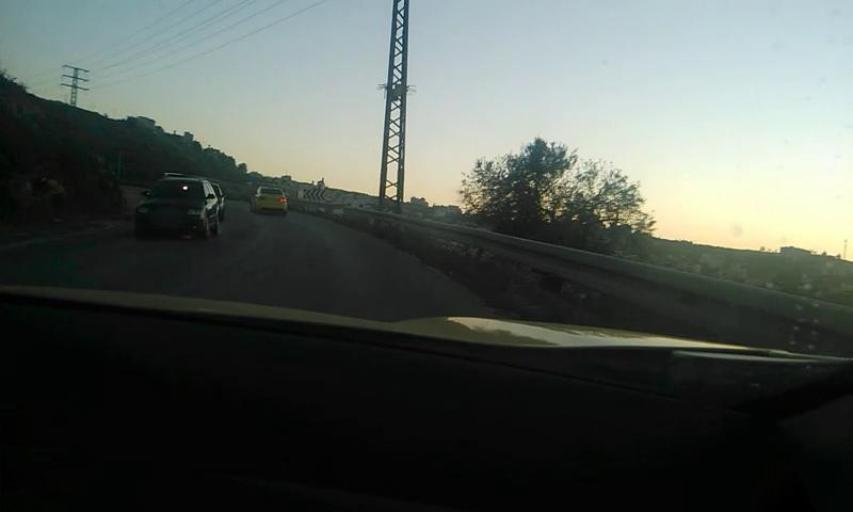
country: PS
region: West Bank
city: Jifna
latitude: 31.9564
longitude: 35.2172
